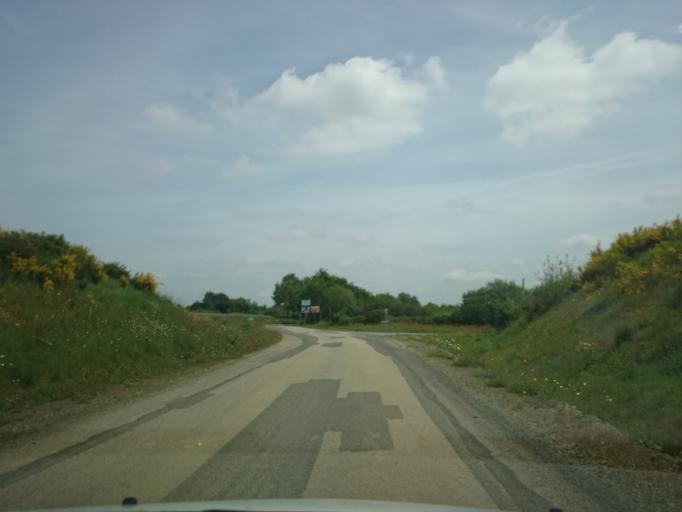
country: FR
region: Pays de la Loire
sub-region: Departement de la Loire-Atlantique
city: La Montagne
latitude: 47.1750
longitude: -1.6899
